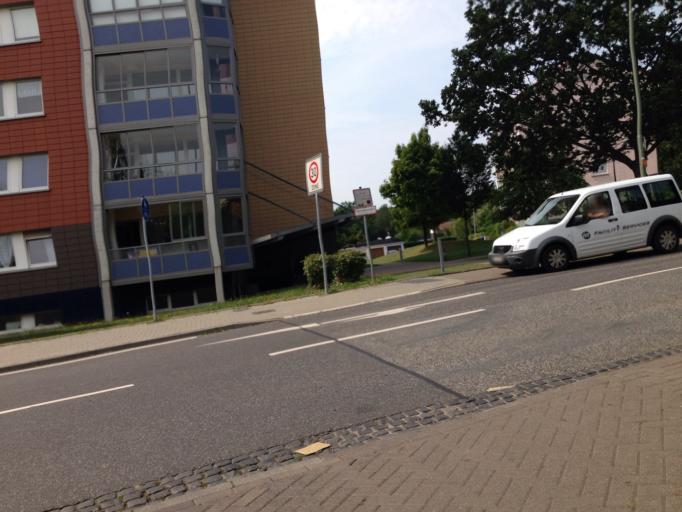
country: DE
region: Hesse
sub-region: Regierungsbezirk Giessen
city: Giessen
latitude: 50.5786
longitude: 8.7062
